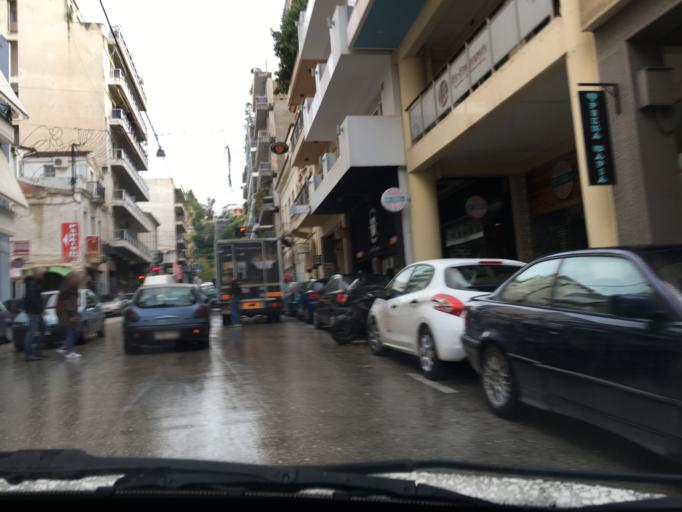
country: GR
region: West Greece
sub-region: Nomos Achaias
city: Patra
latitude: 38.2467
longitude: 21.7377
